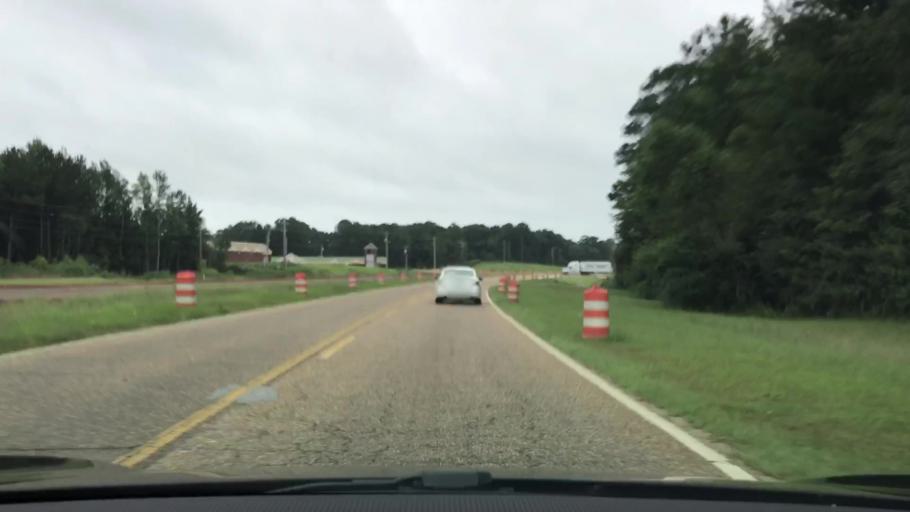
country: US
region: Alabama
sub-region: Coffee County
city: Elba
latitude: 31.4246
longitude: -86.0832
